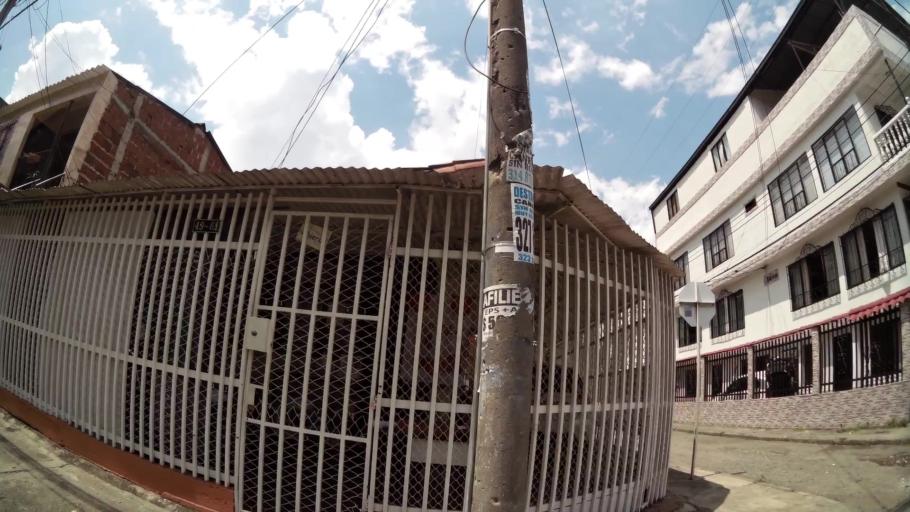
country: CO
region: Valle del Cauca
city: Cali
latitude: 3.4695
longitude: -76.5032
